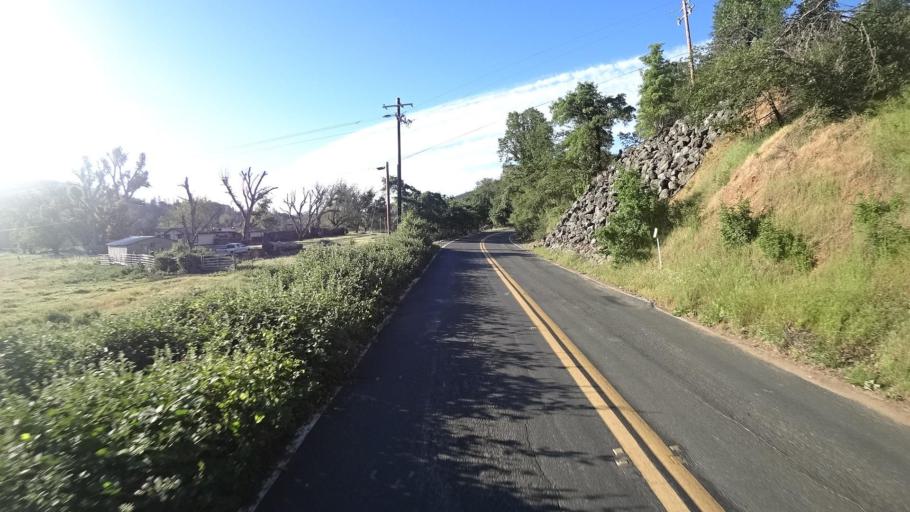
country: US
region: California
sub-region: Lake County
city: Upper Lake
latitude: 39.2129
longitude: -122.9314
